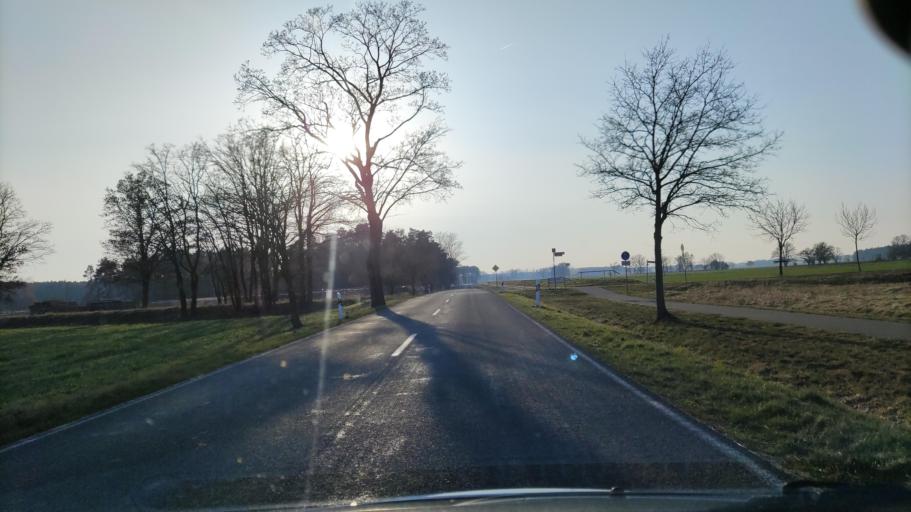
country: DE
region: Brandenburg
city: Lanz
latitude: 52.9933
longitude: 11.5699
